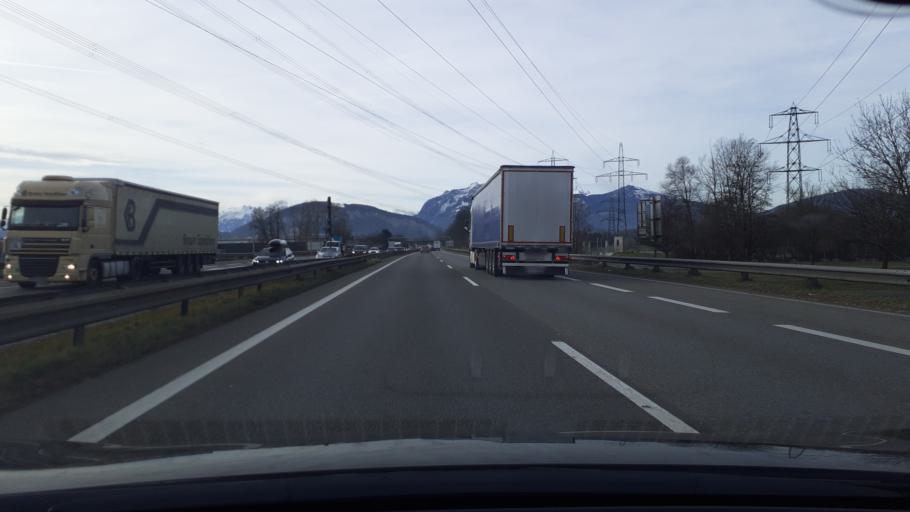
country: AT
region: Vorarlberg
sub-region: Politischer Bezirk Feldkirch
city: Altach
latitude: 47.3662
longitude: 9.6533
